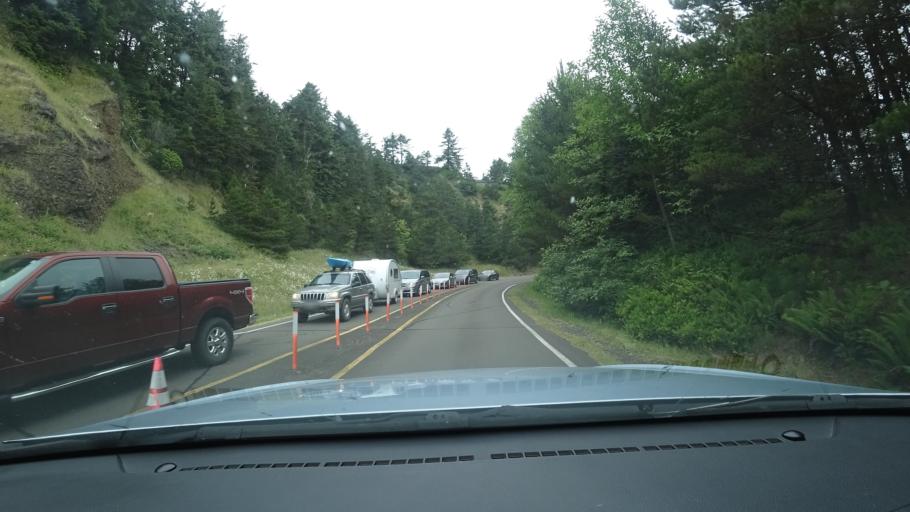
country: US
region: Oregon
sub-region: Lincoln County
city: Newport
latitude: 44.6748
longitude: -124.0649
